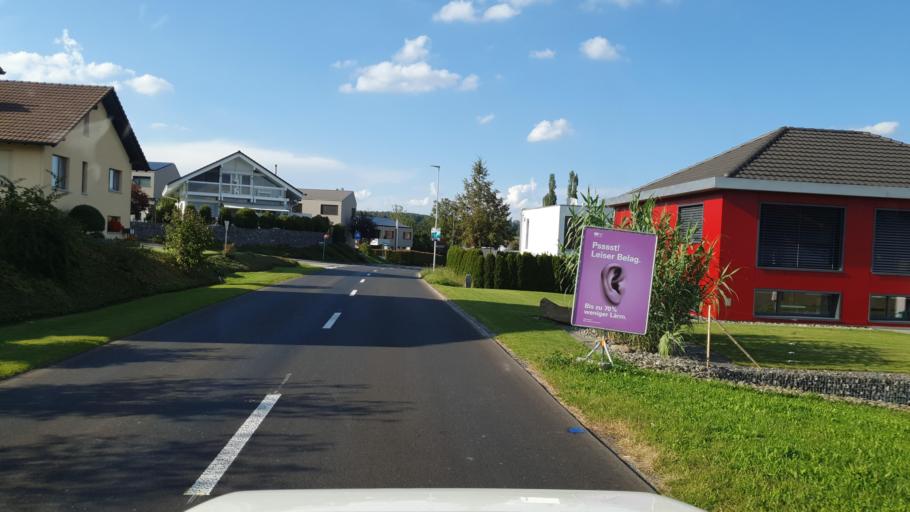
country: CH
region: Aargau
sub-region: Bezirk Muri
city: Auw
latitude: 47.2088
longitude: 8.3612
